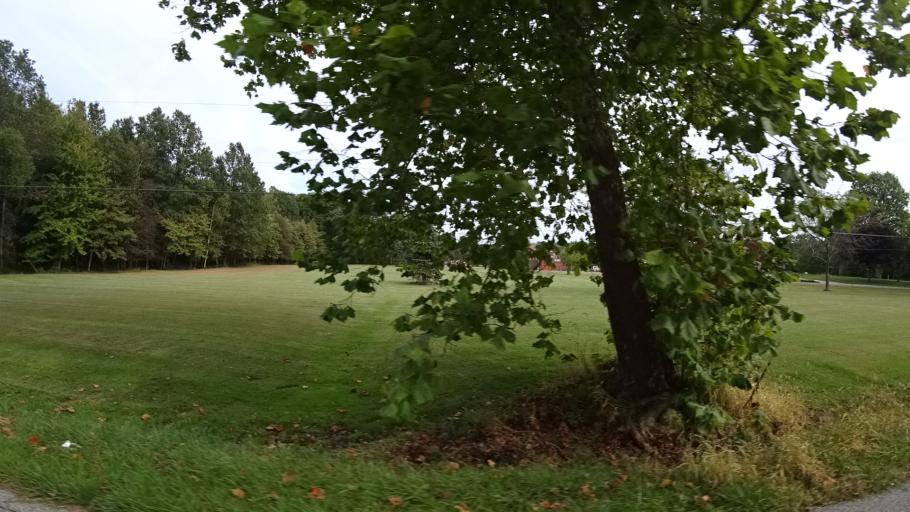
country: US
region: Indiana
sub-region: LaPorte County
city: Long Beach
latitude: 41.7340
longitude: -86.8161
